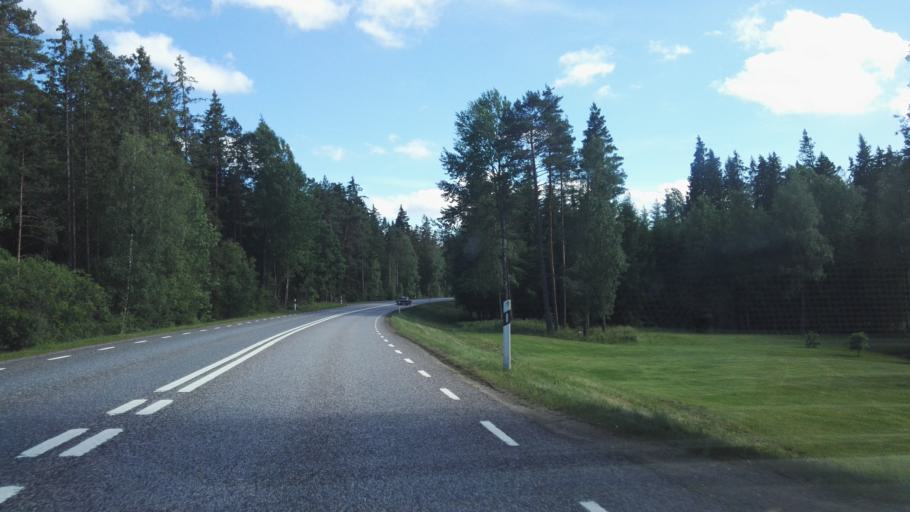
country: SE
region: Kronoberg
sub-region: Vaxjo Kommun
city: Lammhult
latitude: 57.2341
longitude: 14.5093
